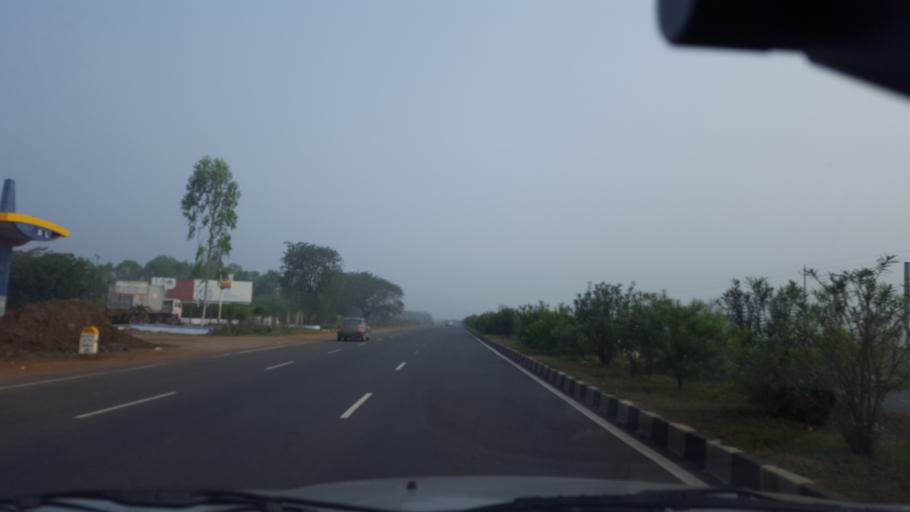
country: IN
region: Andhra Pradesh
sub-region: Prakasam
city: Ongole
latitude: 15.4361
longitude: 80.0447
